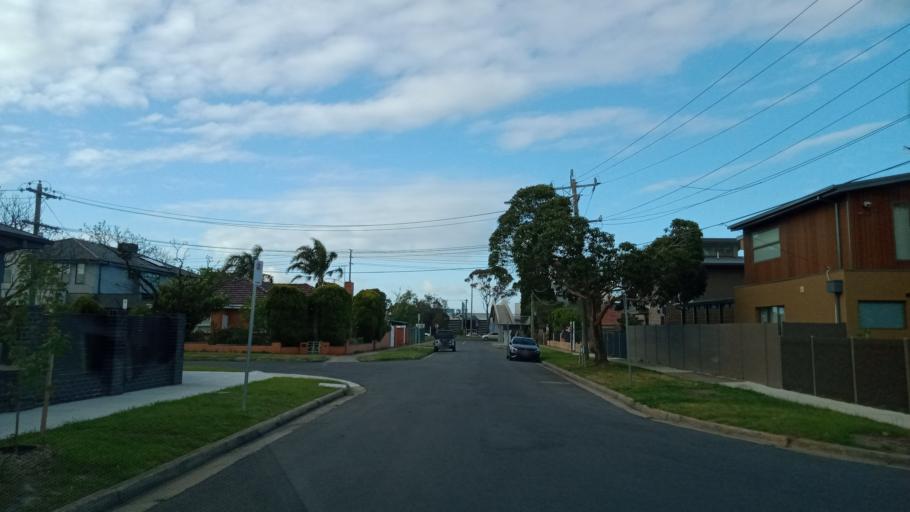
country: AU
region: Victoria
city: Highett
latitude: -37.9339
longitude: 145.0517
